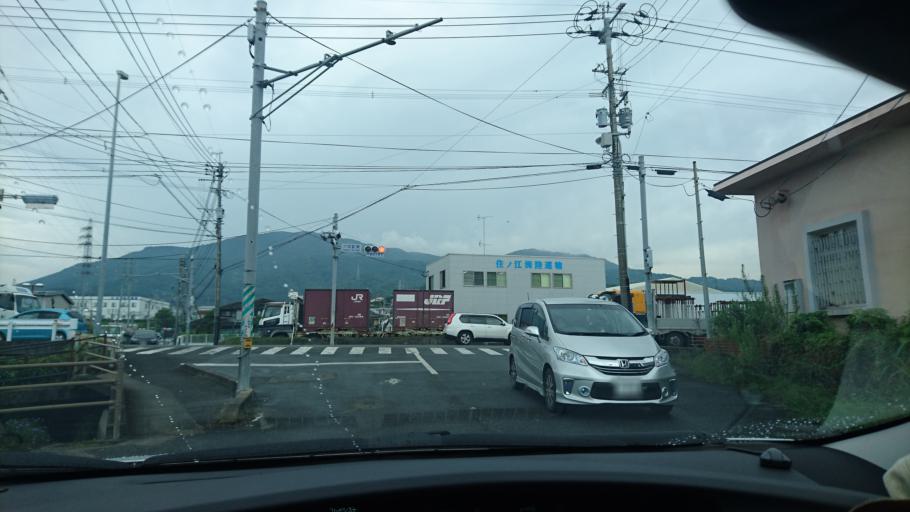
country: JP
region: Saga Prefecture
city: Takeocho-takeo
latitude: 33.2125
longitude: 130.1104
